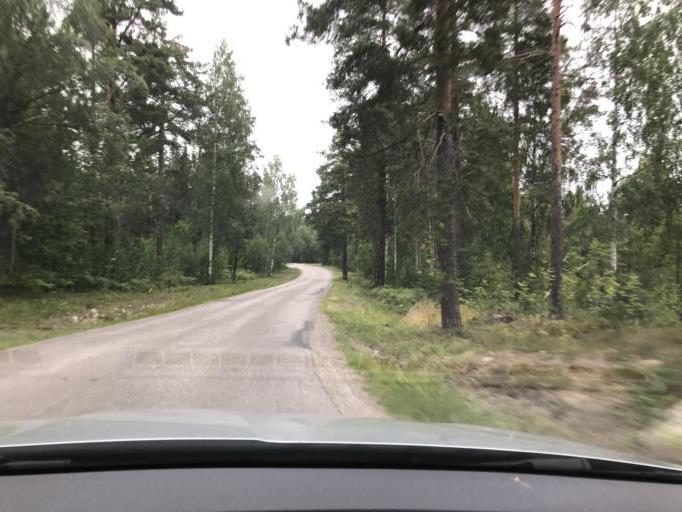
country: SE
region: Vaesternorrland
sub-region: Sundsvalls Kommun
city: Sundsvall
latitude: 62.4018
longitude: 17.3081
